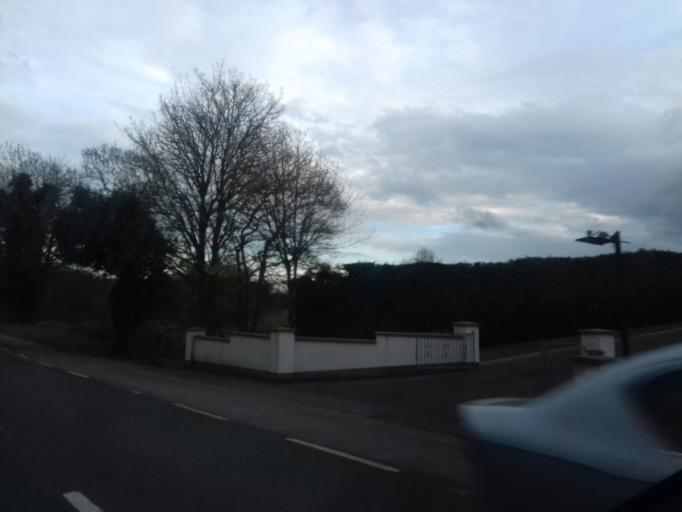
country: IE
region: Ulster
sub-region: An Cabhan
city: Ballyconnell
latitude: 54.1024
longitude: -7.5662
